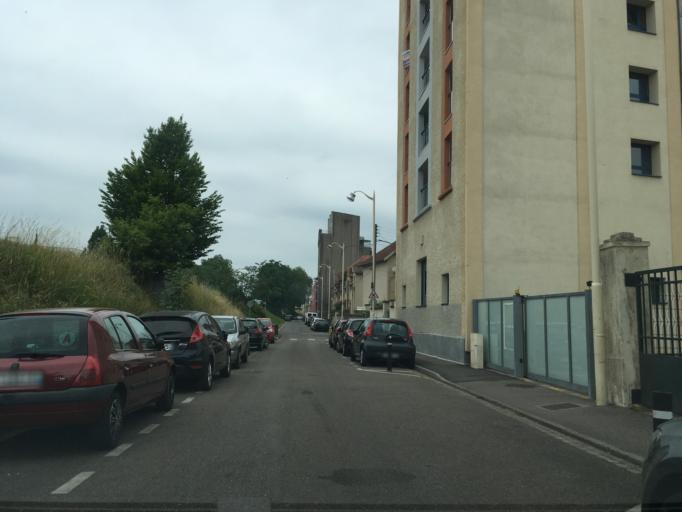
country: FR
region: Lorraine
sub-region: Departement de Meurthe-et-Moselle
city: Nancy
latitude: 48.6970
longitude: 6.1912
